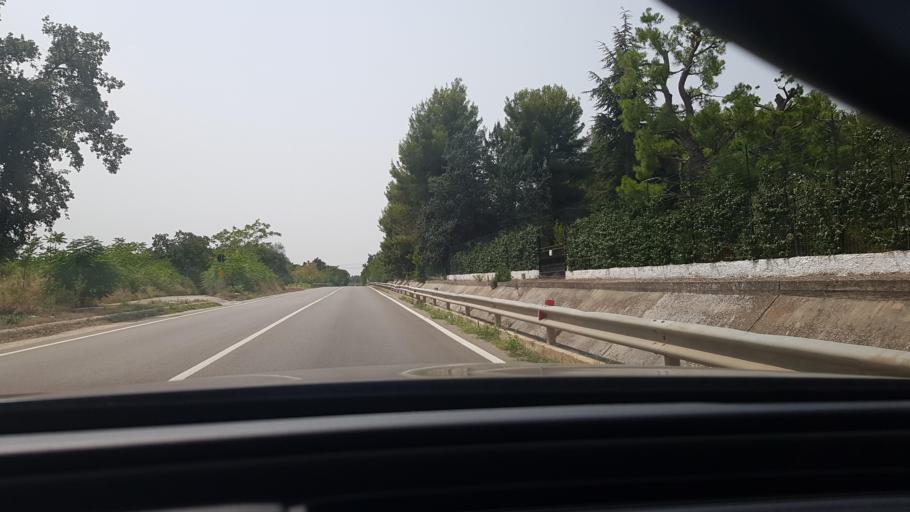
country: IT
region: Apulia
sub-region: Provincia di Barletta - Andria - Trani
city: Andria
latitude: 41.1548
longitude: 16.2941
